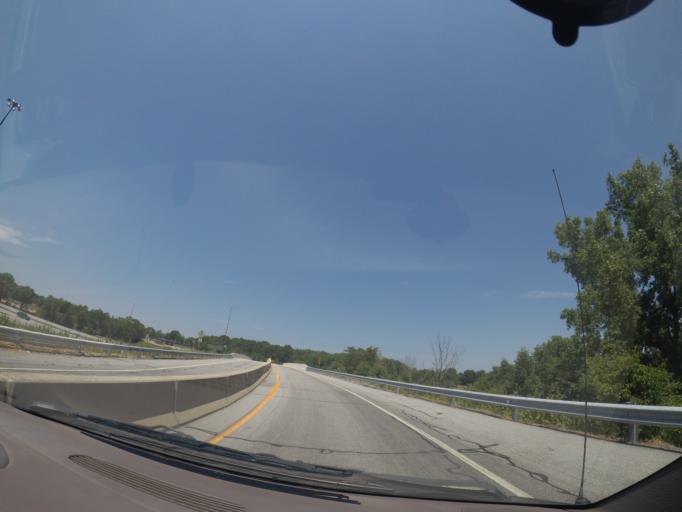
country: US
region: Indiana
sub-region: LaPorte County
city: LaPorte
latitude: 41.6655
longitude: -86.7311
